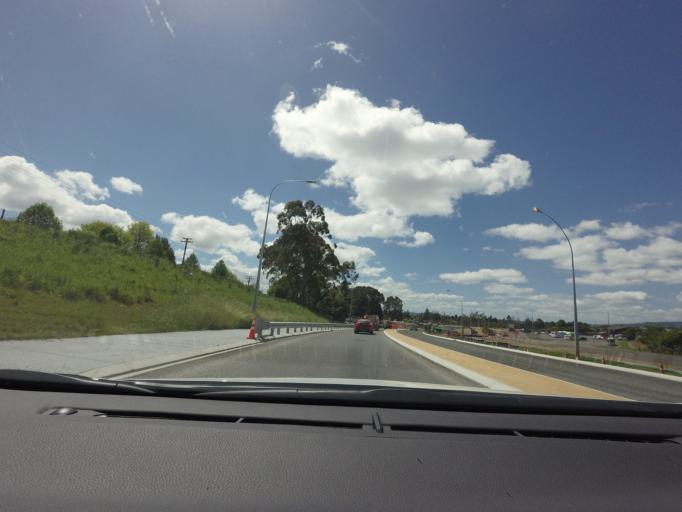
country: NZ
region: Bay of Plenty
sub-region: Rotorua District
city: Rotorua
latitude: -38.1671
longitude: 176.2454
